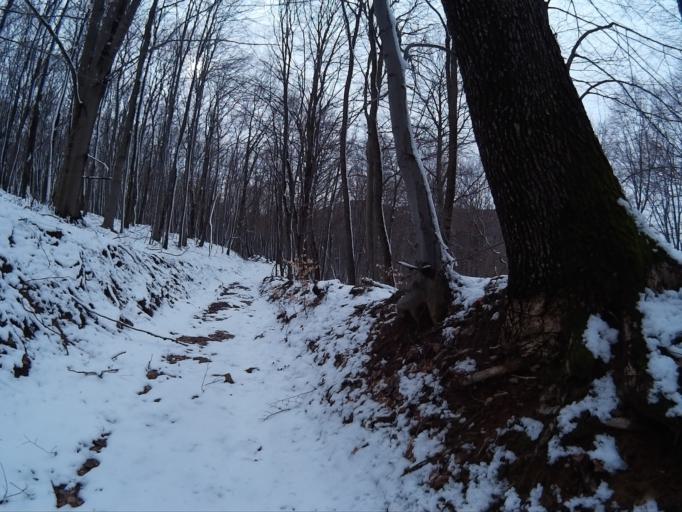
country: HU
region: Borsod-Abauj-Zemplen
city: Gonc
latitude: 48.4166
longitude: 21.3567
